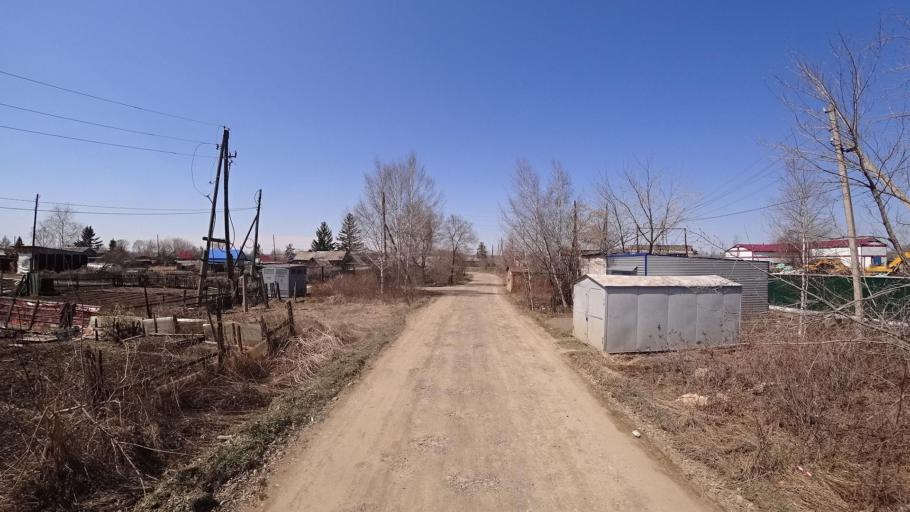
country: RU
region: Khabarovsk Krai
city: Khurba
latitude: 50.4066
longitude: 136.8897
